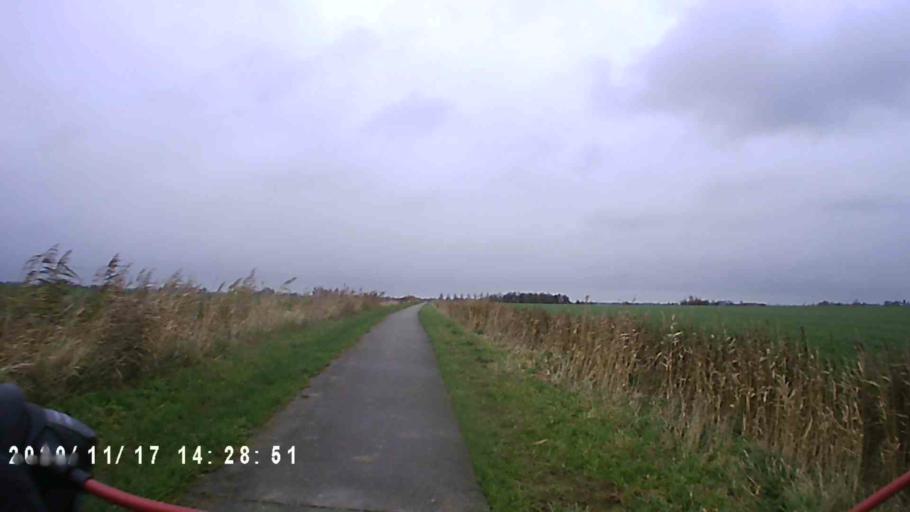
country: NL
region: Groningen
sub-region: Gemeente Zuidhorn
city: Grijpskerk
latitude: 53.2723
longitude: 6.3500
